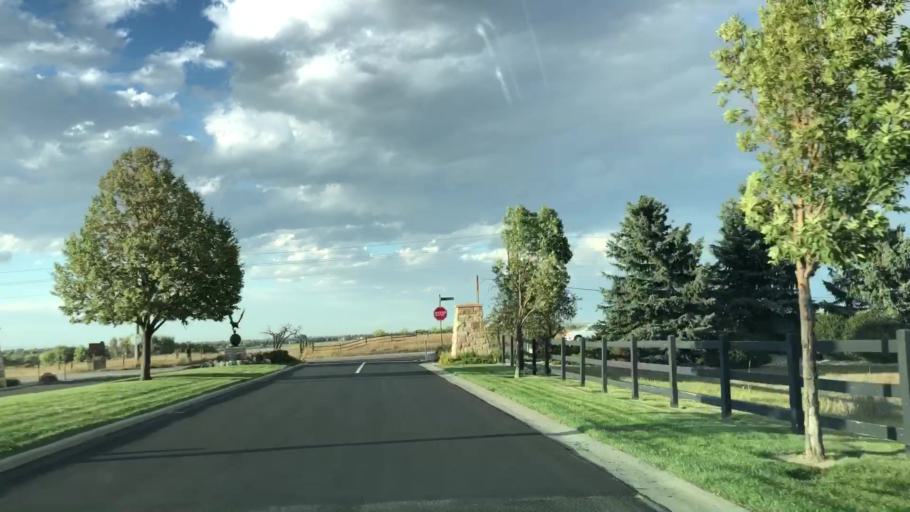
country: US
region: Colorado
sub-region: Larimer County
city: Loveland
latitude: 40.4791
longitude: -105.0082
